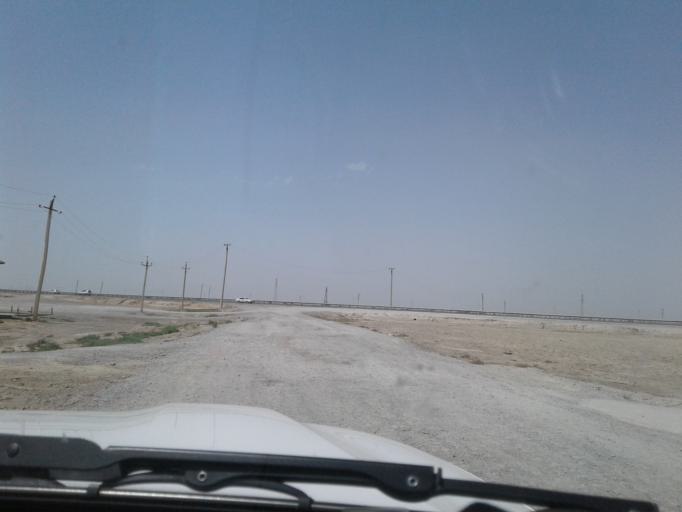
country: IR
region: Razavi Khorasan
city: Kalat-e Naderi
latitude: 37.2059
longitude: 60.0230
